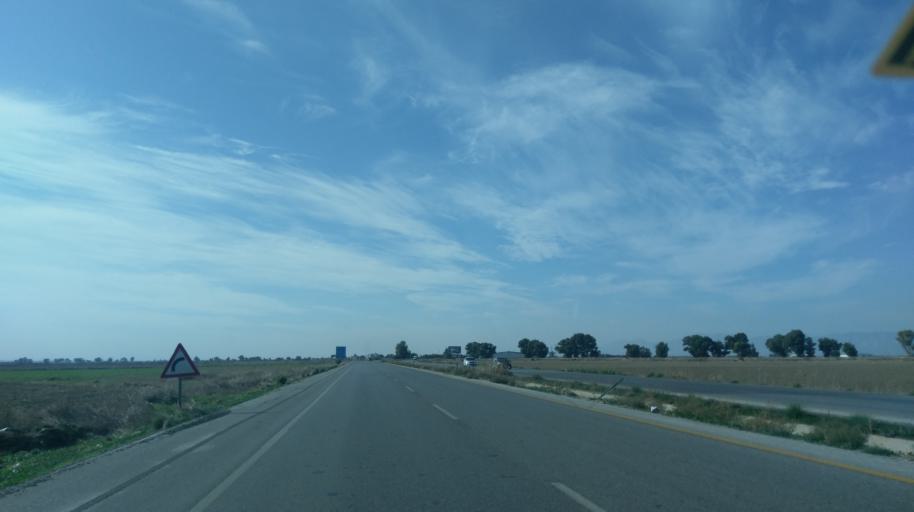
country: CY
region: Ammochostos
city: Lefkonoiko
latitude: 35.1714
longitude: 33.7804
